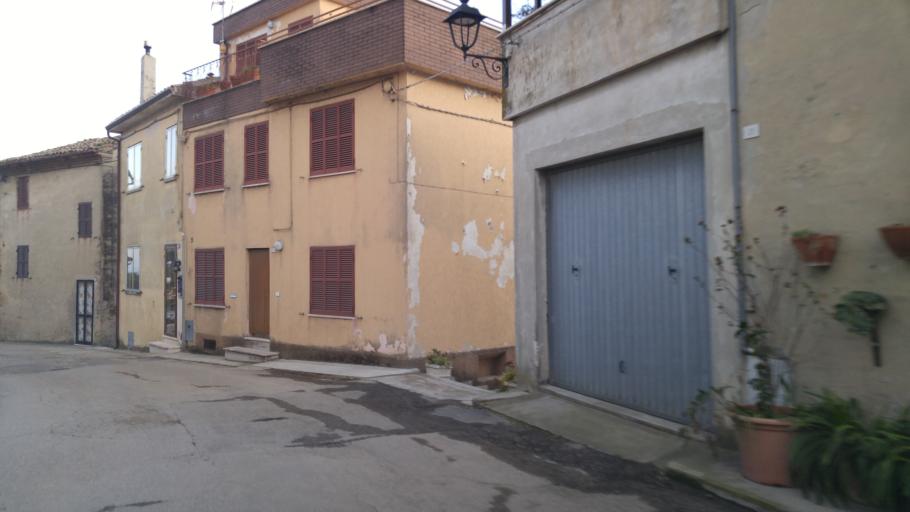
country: IT
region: The Marches
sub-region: Provincia di Pesaro e Urbino
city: Monte Porzio
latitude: 43.6908
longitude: 13.0466
